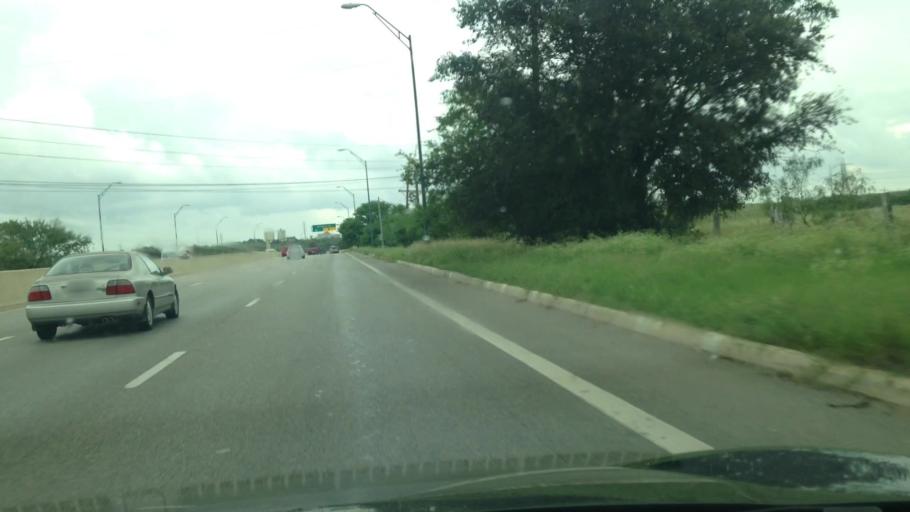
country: US
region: Texas
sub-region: Bexar County
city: Alamo Heights
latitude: 29.5470
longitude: -98.4472
